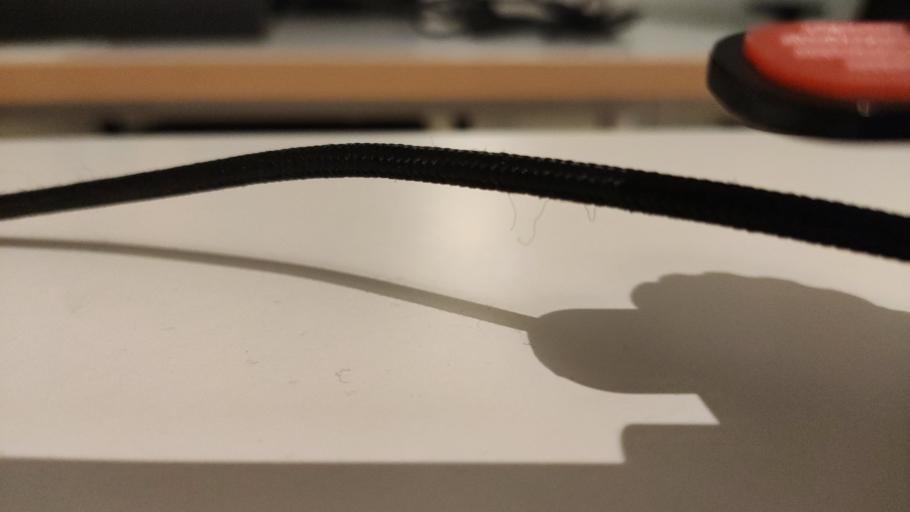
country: RU
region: Moskovskaya
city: Novosin'kovo
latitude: 56.3720
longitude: 37.3620
